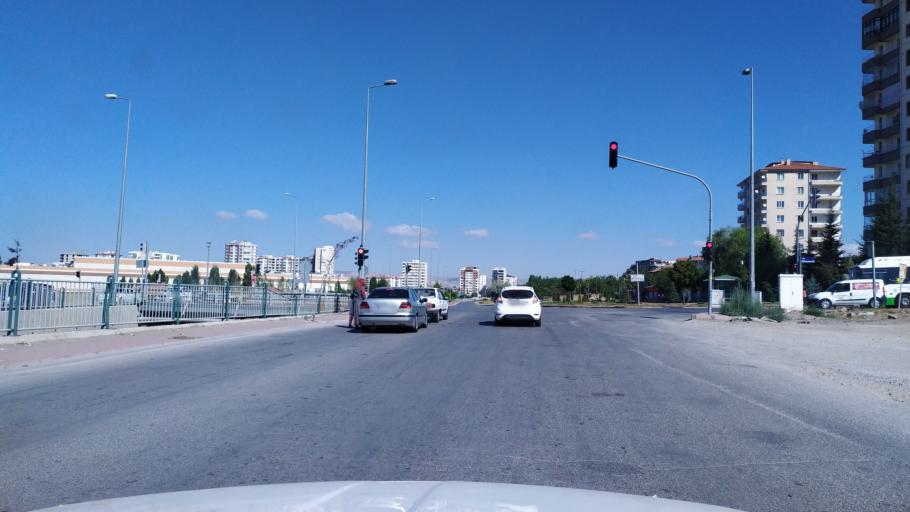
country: TR
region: Kayseri
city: Kocasinan
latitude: 38.7374
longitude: 35.5451
